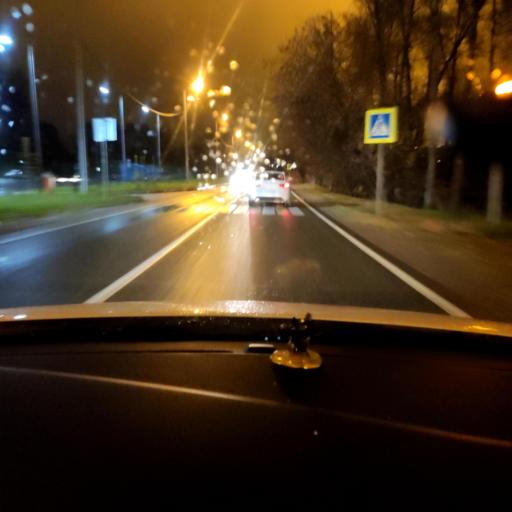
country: RU
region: Tatarstan
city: Osinovo
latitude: 55.8430
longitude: 48.8918
